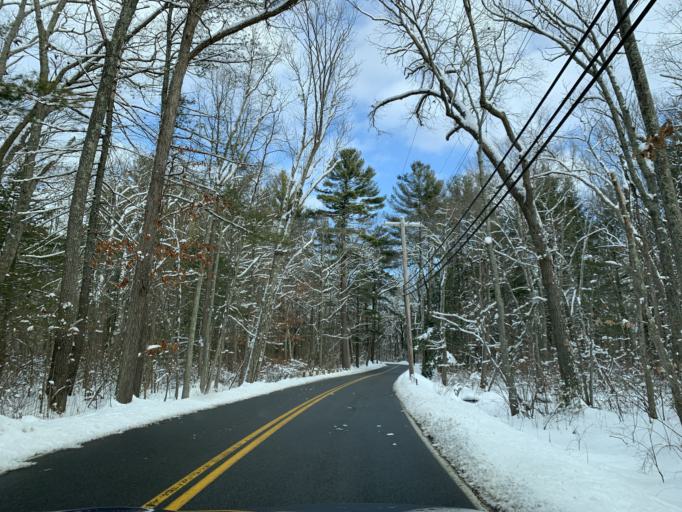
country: US
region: Massachusetts
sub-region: Norfolk County
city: Dover
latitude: 42.2588
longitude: -71.2792
